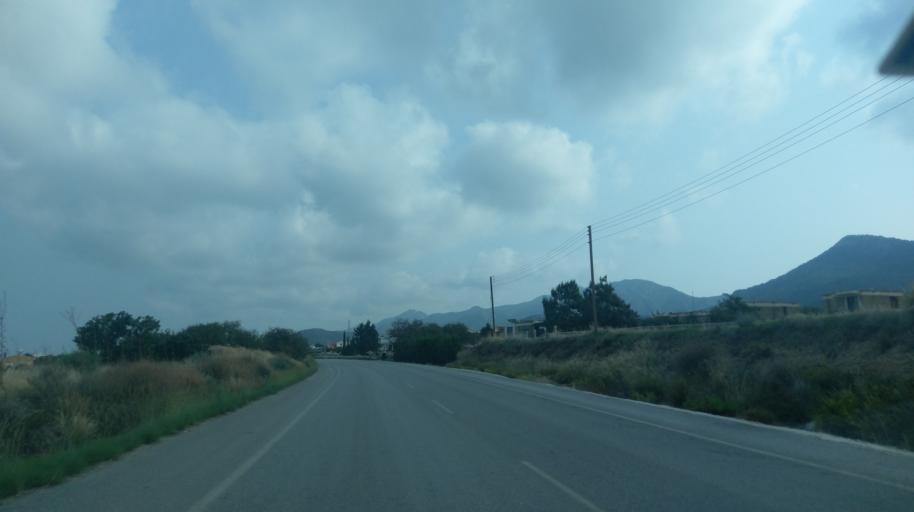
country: CY
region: Ammochostos
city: Lefkonoiko
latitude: 35.3629
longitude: 33.6768
